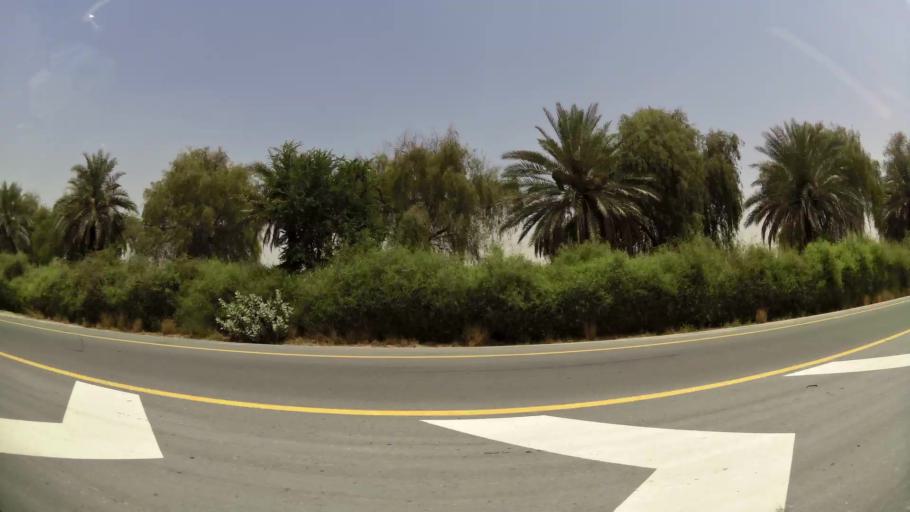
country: AE
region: Dubai
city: Dubai
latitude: 25.0579
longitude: 55.2636
